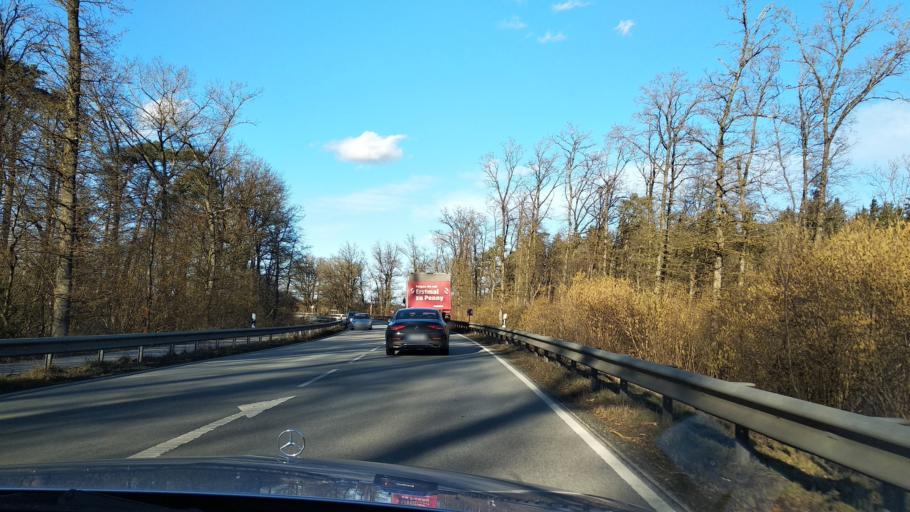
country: DE
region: Bavaria
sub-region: Upper Bavaria
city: Ampfing
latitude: 48.2312
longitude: 12.4137
